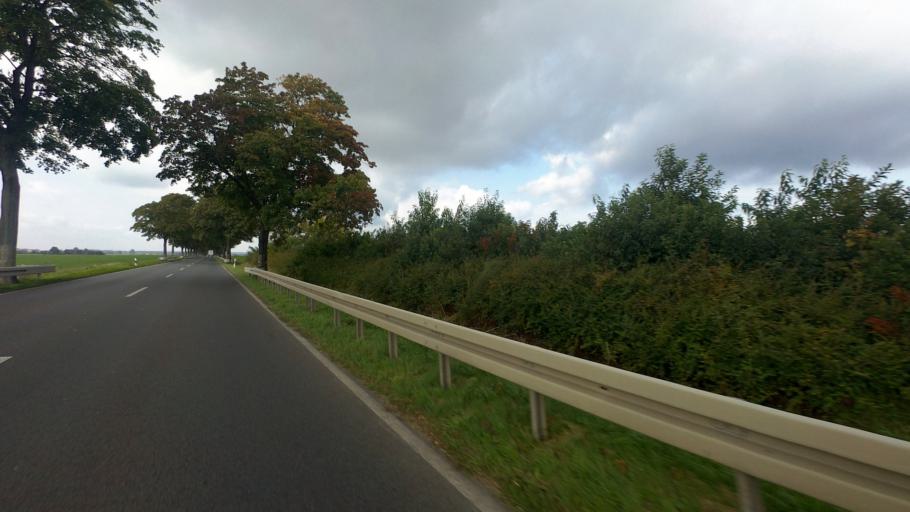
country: DE
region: Brandenburg
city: Plessa
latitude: 51.4665
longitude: 13.6001
